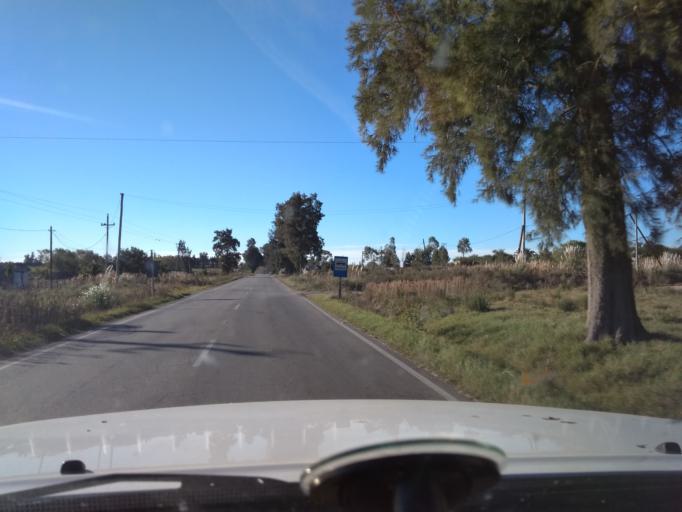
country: UY
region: Canelones
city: San Bautista
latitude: -34.4089
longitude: -55.9598
